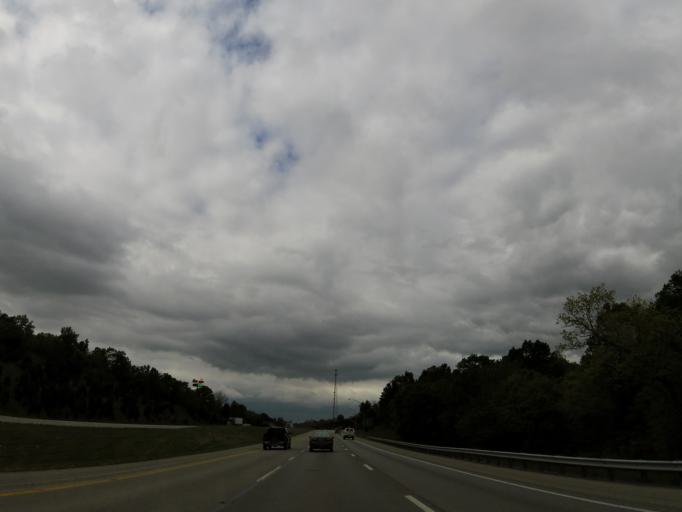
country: US
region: Kentucky
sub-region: Scott County
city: Georgetown
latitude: 38.3734
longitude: -84.5702
